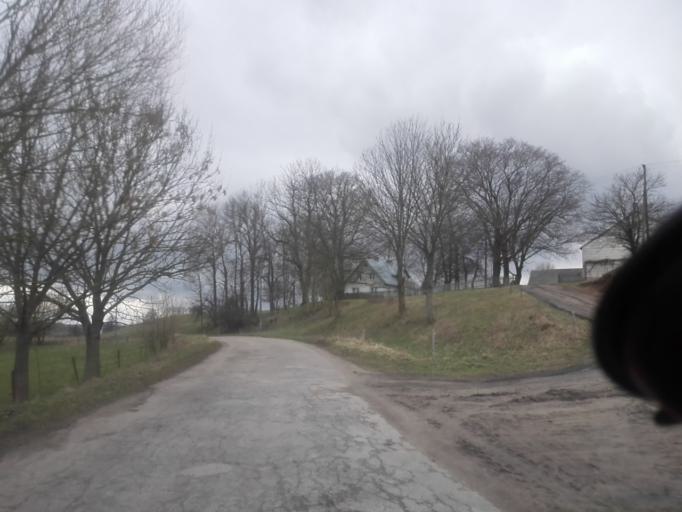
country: PL
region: Podlasie
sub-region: Suwalki
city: Suwalki
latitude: 54.2538
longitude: 23.0017
